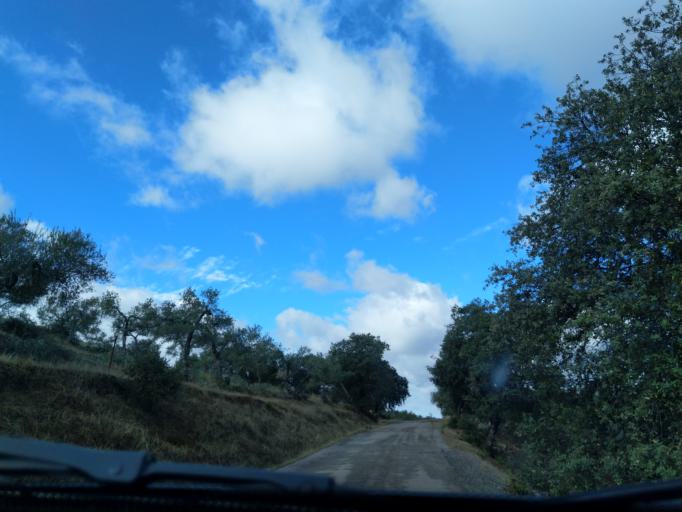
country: ES
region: Extremadura
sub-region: Provincia de Badajoz
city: Reina
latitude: 38.1291
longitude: -5.9343
